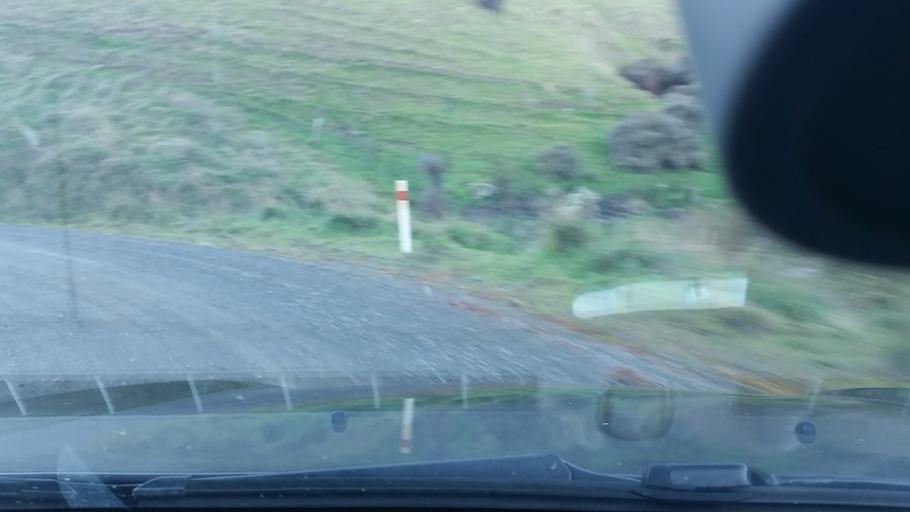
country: NZ
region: Marlborough
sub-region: Marlborough District
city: Blenheim
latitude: -41.7504
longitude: 174.0592
